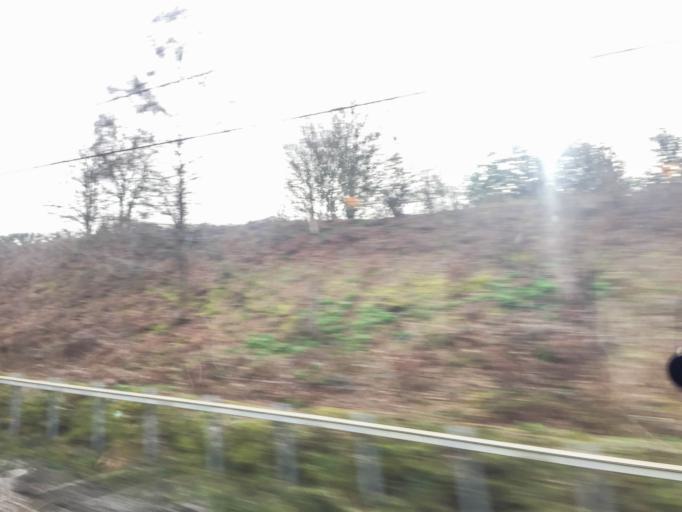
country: GB
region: England
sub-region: Borough of Halton
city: Daresbury
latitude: 53.3541
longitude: -2.6388
